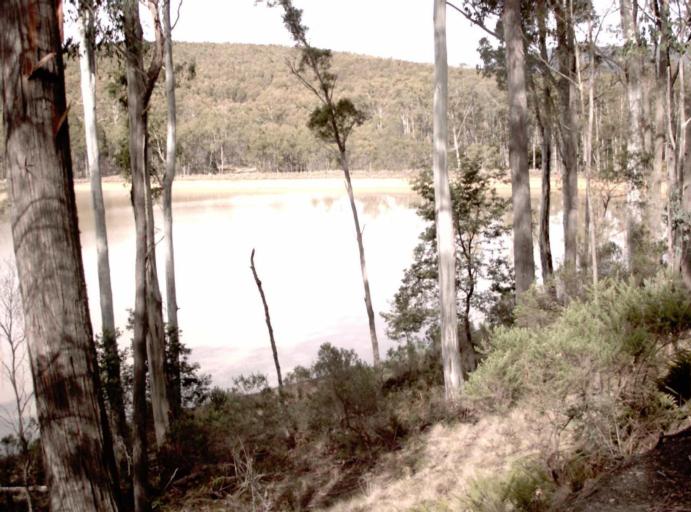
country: AU
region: Tasmania
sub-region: Northern Midlands
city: Evandale
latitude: -41.4581
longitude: 147.4723
